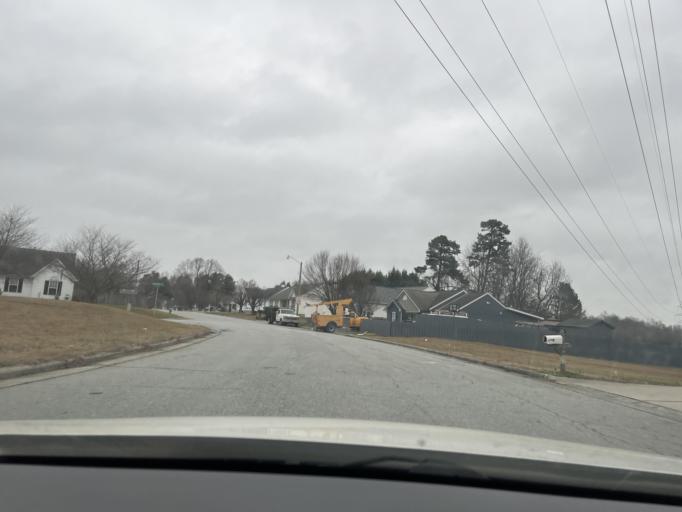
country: US
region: North Carolina
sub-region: Guilford County
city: Pleasant Garden
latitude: 36.0053
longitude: -79.7950
